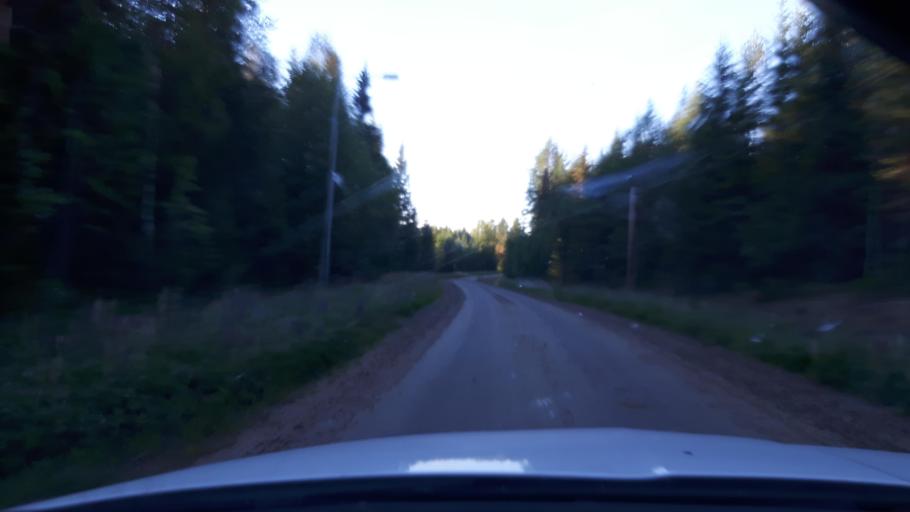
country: SE
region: Vaesternorrland
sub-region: Ange Kommun
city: Ange
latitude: 62.1450
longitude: 15.6604
